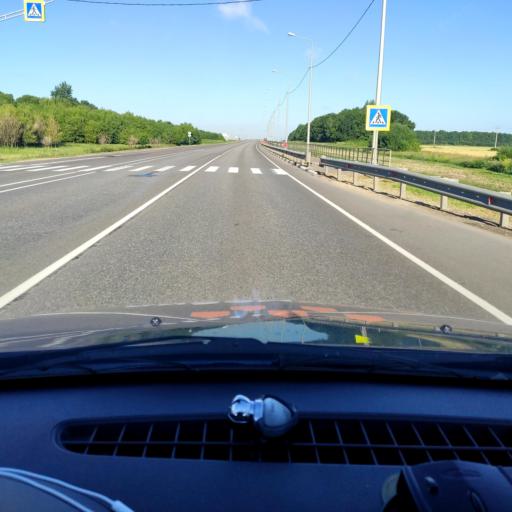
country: RU
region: Orjol
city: Pokrovskoye
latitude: 52.6223
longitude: 36.7853
